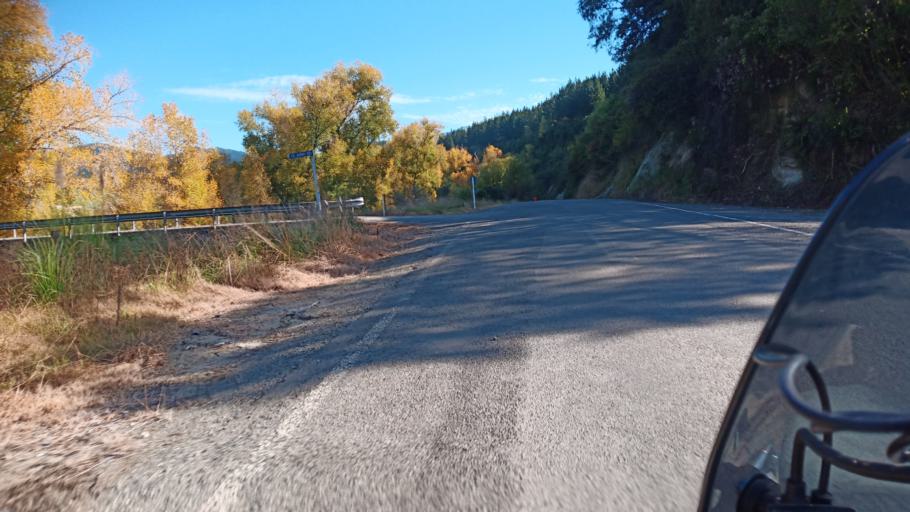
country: NZ
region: Hawke's Bay
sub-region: Wairoa District
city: Wairoa
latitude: -38.9234
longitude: 177.2612
